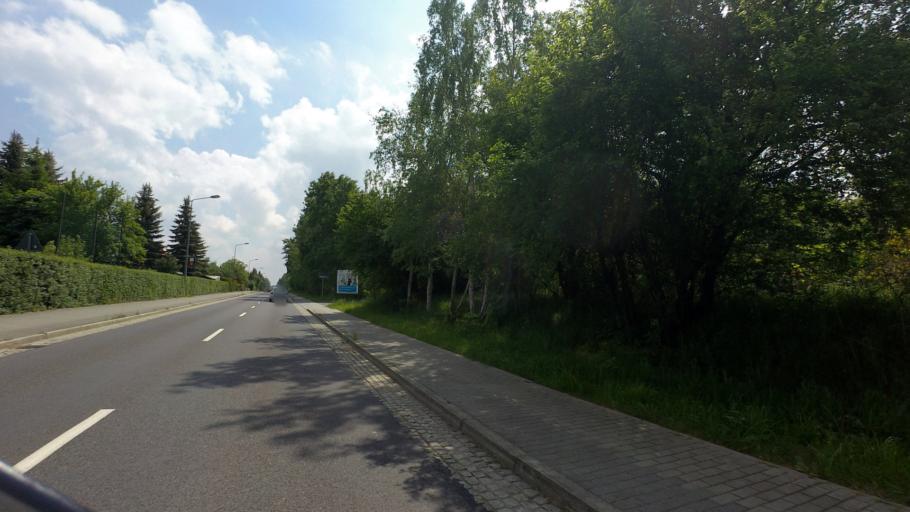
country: DE
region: Saxony
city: Weisswasser
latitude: 51.5180
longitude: 14.6074
